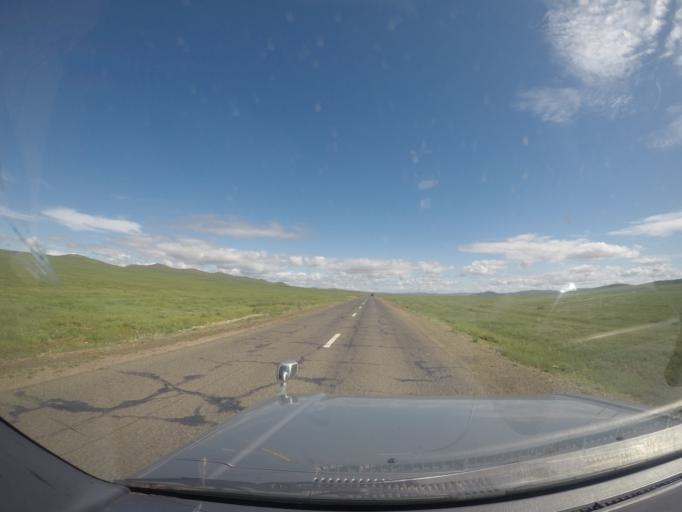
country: MN
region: Hentiy
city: Avraga
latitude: 47.5193
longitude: 109.4194
